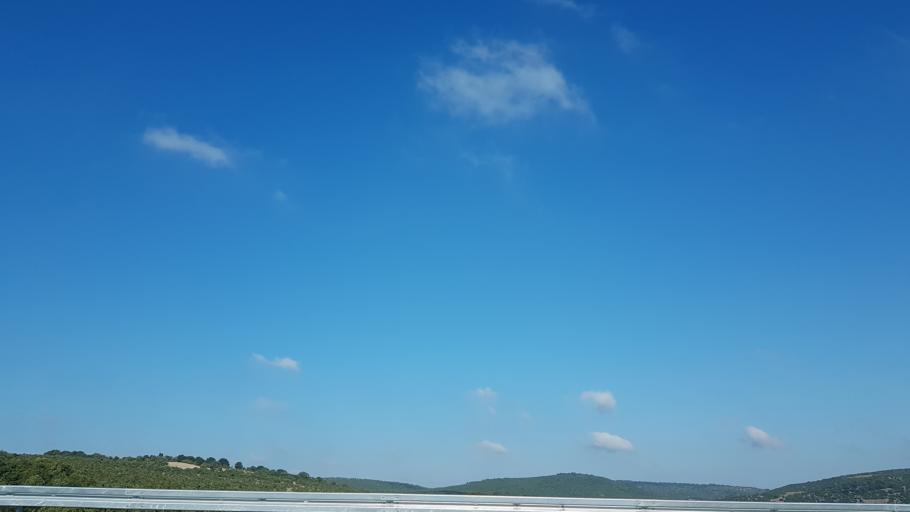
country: TR
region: Balikesir
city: Ertugrul
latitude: 39.5384
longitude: 27.6757
